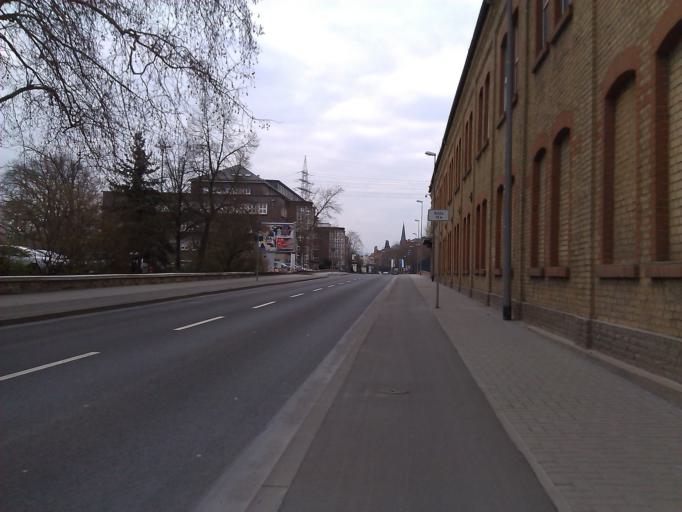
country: DE
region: Hesse
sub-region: Regierungsbezirk Darmstadt
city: Wiesbaden
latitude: 50.0328
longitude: 8.2481
